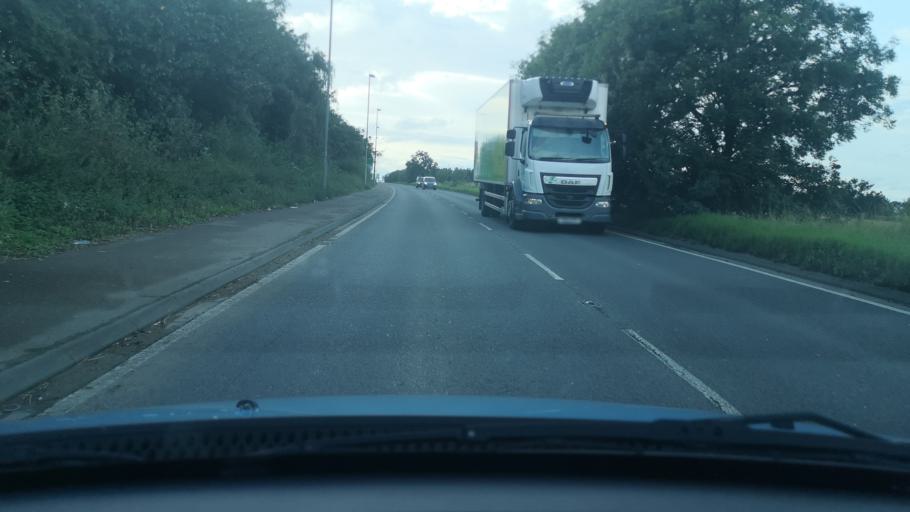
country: GB
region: England
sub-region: City and Borough of Wakefield
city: North Elmsall
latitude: 53.6053
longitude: -1.2717
